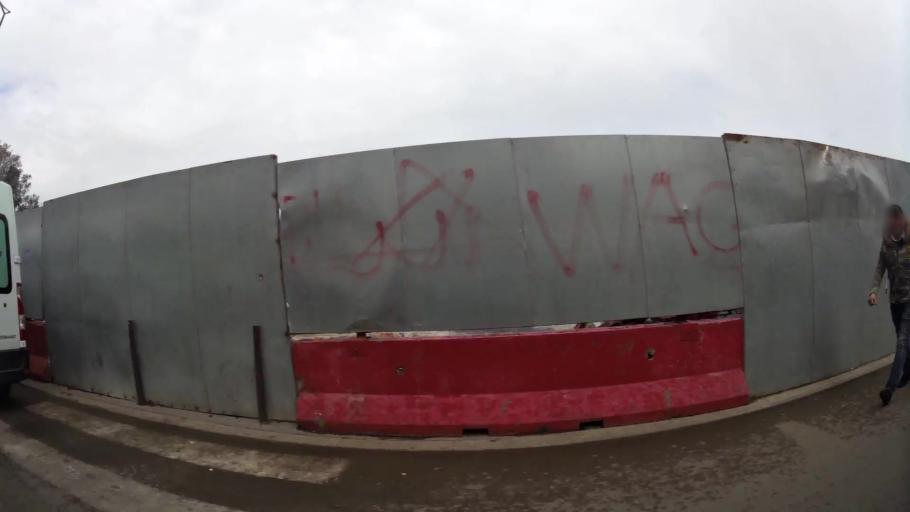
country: MA
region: Grand Casablanca
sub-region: Casablanca
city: Casablanca
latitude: 33.5894
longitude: -7.6203
